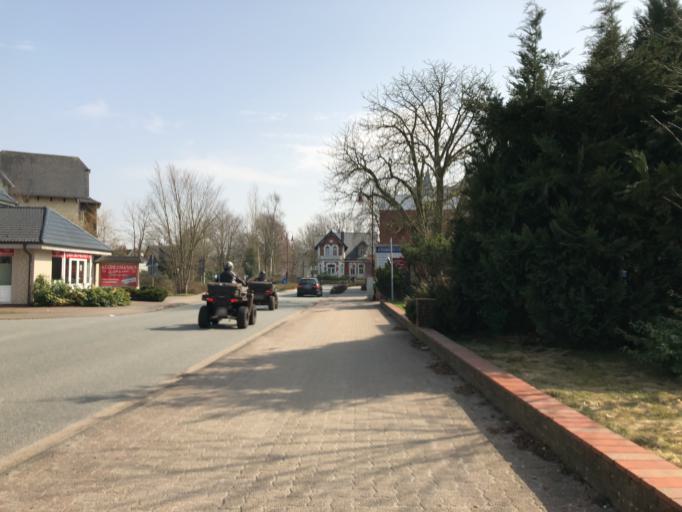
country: DE
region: Schleswig-Holstein
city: Tarp
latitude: 54.6648
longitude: 9.3997
